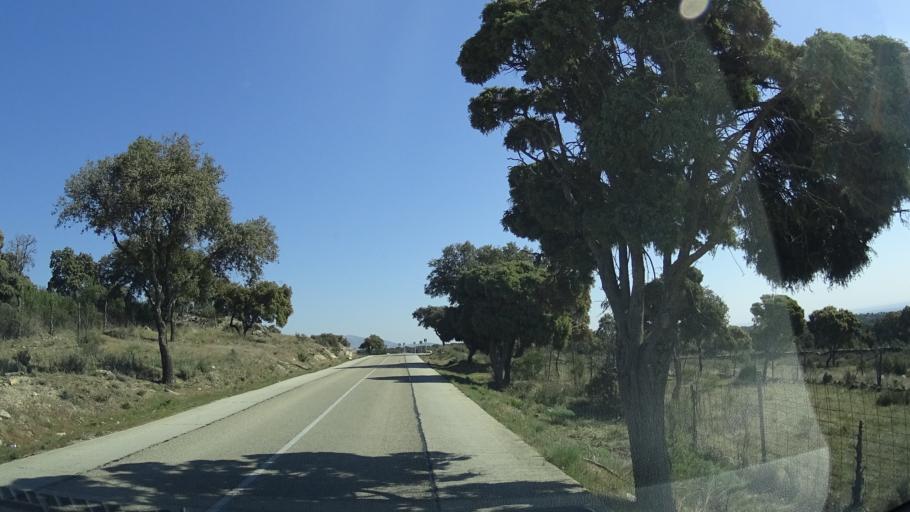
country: ES
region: Madrid
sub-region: Provincia de Madrid
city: Hoyo de Manzanares
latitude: 40.6392
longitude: -3.8488
